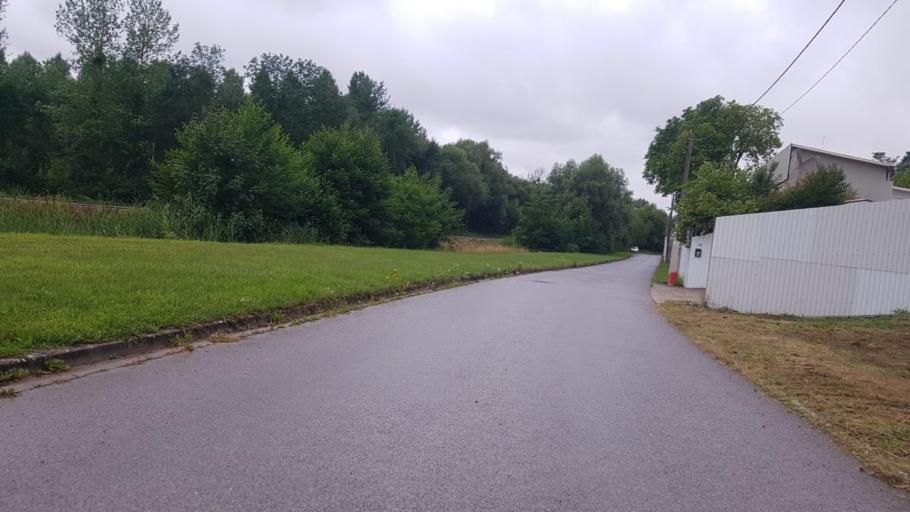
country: FR
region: Champagne-Ardenne
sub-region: Departement de la Marne
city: Vitry-le-Francois
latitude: 48.7501
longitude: 4.5721
